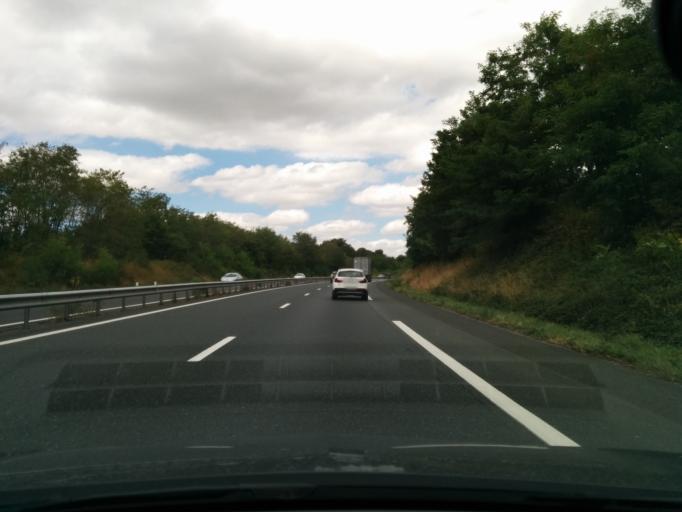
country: FR
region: Centre
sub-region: Departement de l'Indre
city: Luant
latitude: 46.7392
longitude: 1.6136
